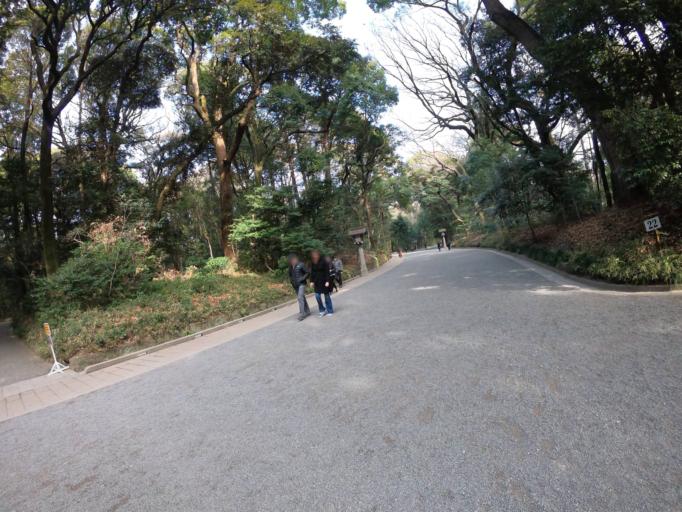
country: JP
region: Chiba
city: Ichihara
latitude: 35.4614
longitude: 140.0162
